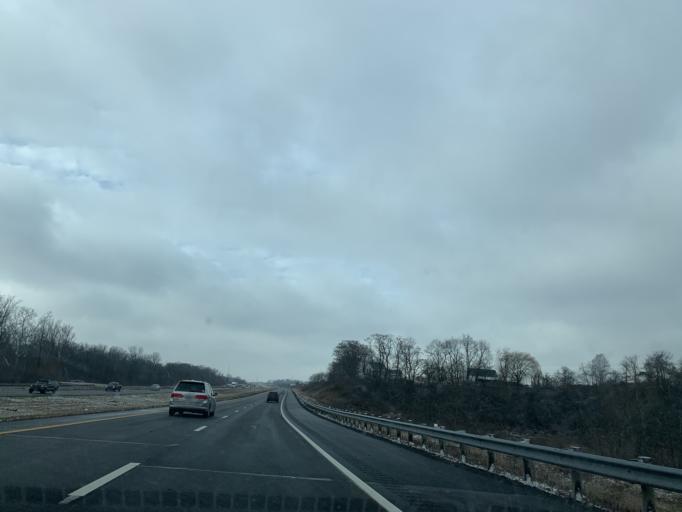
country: US
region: Ohio
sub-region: Licking County
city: Beechwood Trails
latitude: 40.0727
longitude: -82.6312
